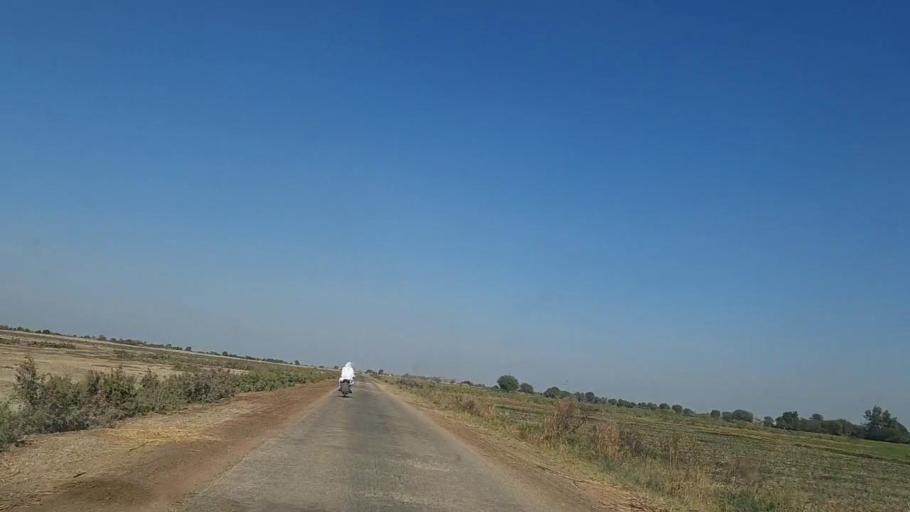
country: PK
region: Sindh
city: Digri
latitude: 25.1462
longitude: 69.0152
